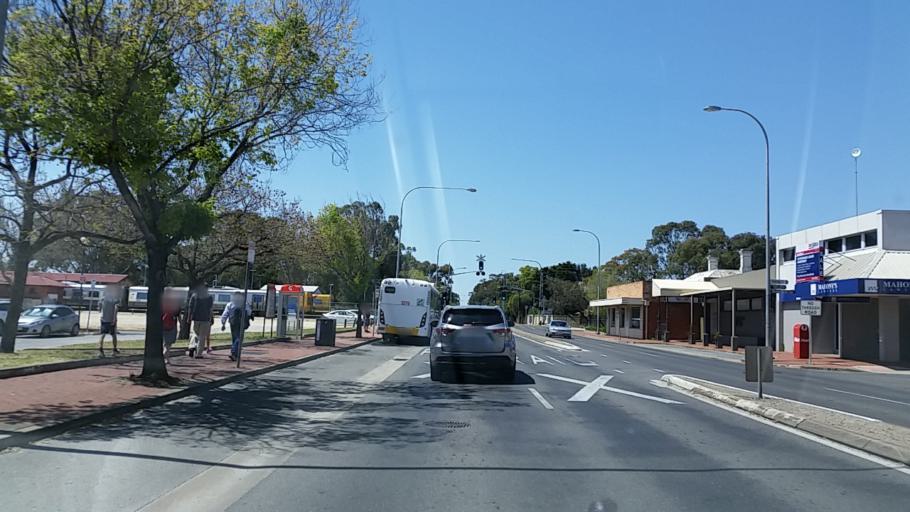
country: AU
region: South Australia
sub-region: Charles Sturt
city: Woodville North
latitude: -34.8783
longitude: 138.5375
